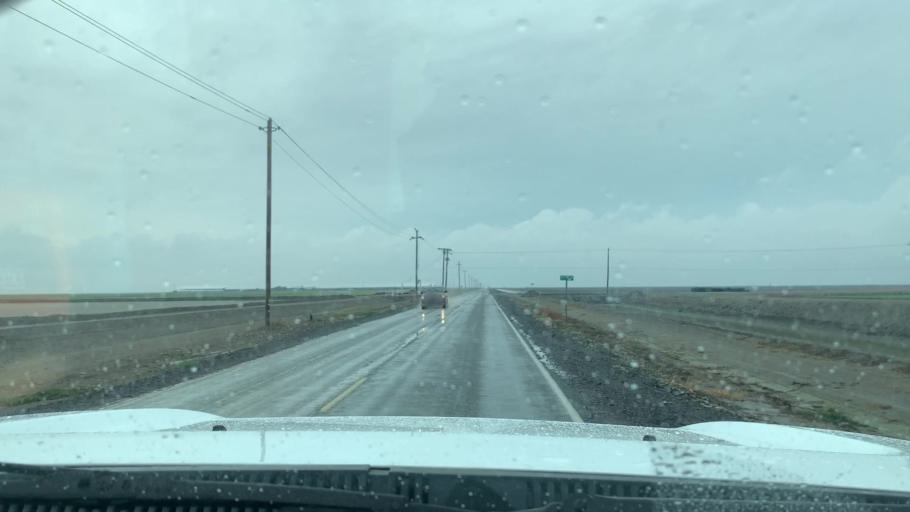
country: US
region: California
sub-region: Tulare County
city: Alpaugh
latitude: 35.9507
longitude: -119.5731
